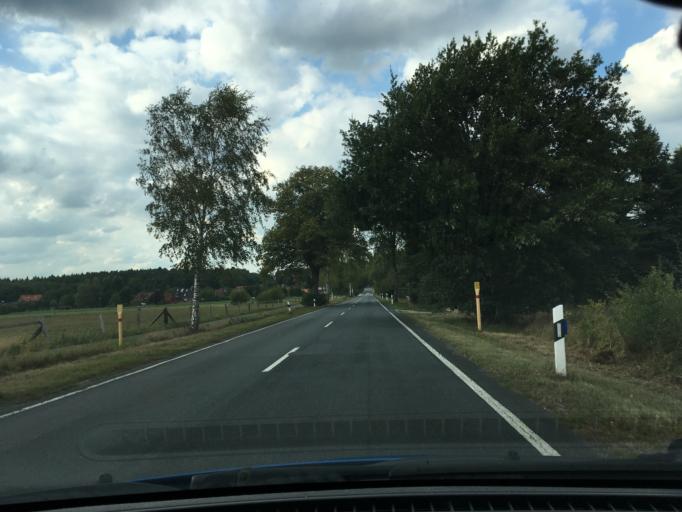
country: DE
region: Lower Saxony
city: Garstedt
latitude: 53.2781
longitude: 10.1641
